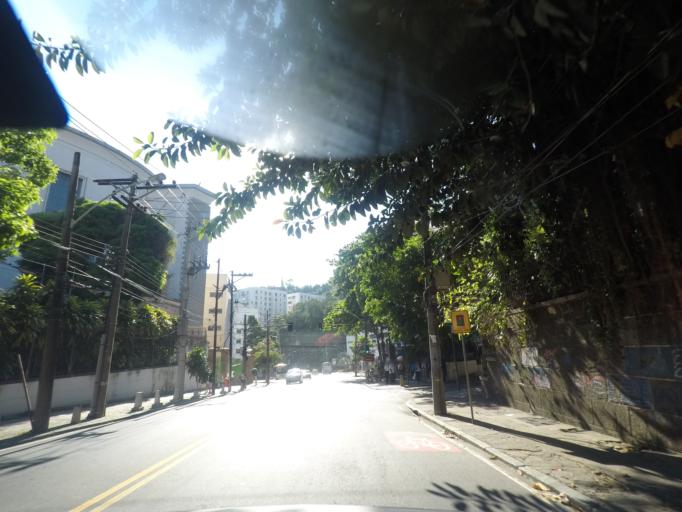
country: BR
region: Rio de Janeiro
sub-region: Rio De Janeiro
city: Rio de Janeiro
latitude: -22.9401
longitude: -43.1989
